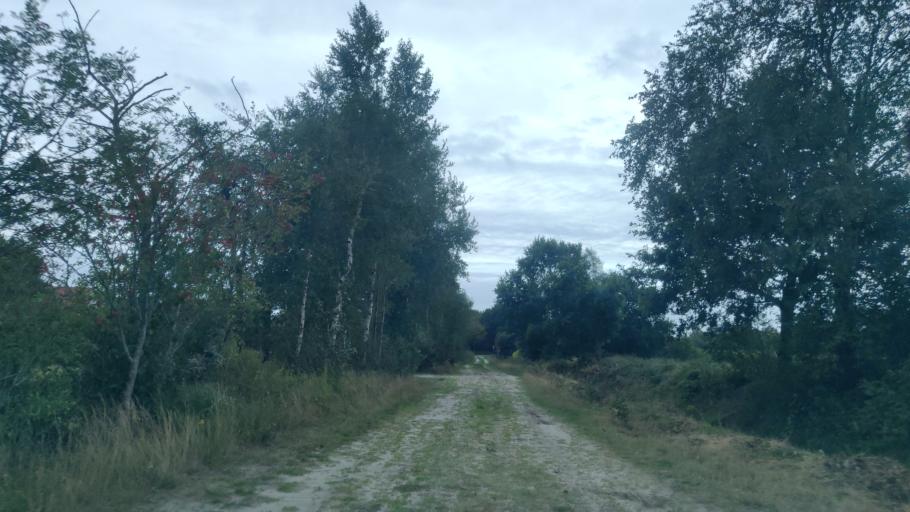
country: DE
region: Lower Saxony
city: Aurich
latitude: 53.5288
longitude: 7.4779
